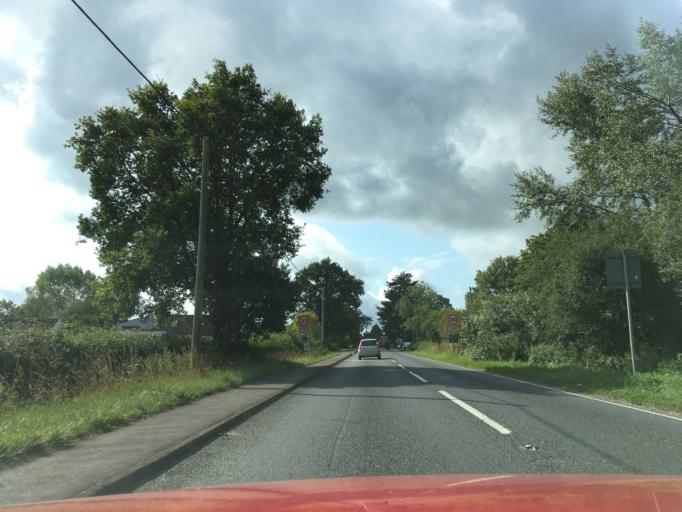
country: GB
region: England
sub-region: Hampshire
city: Bishops Waltham
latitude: 50.9403
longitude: -1.2021
